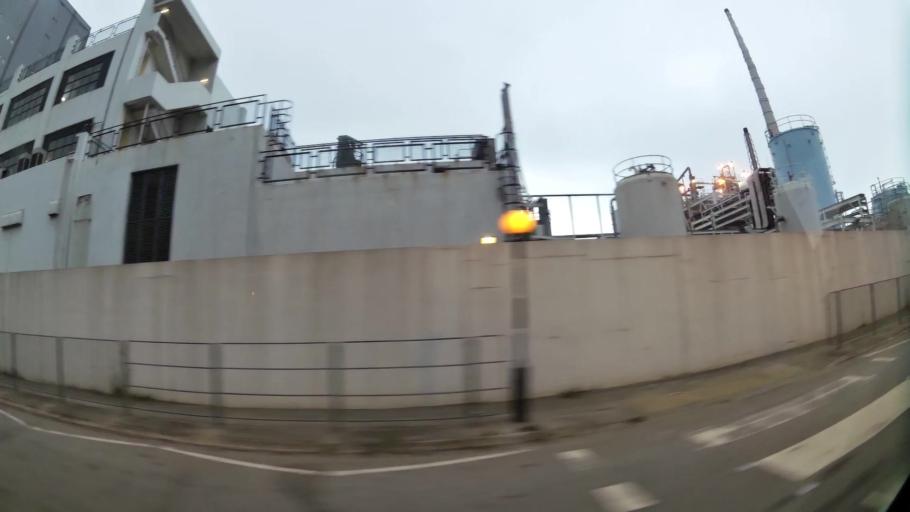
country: HK
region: Tsuen Wan
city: Tsuen Wan
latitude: 22.3311
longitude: 114.1070
